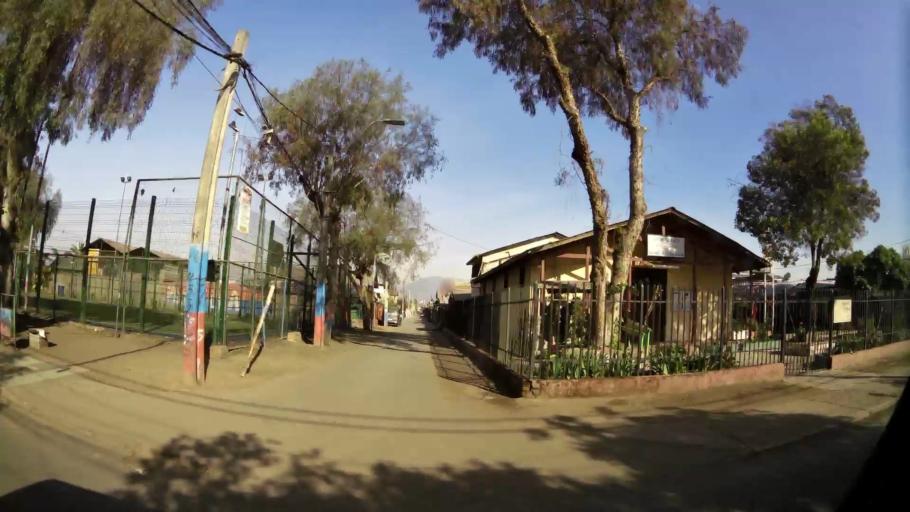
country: CL
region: Santiago Metropolitan
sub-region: Provincia de Santiago
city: Lo Prado
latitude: -33.4179
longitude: -70.7601
